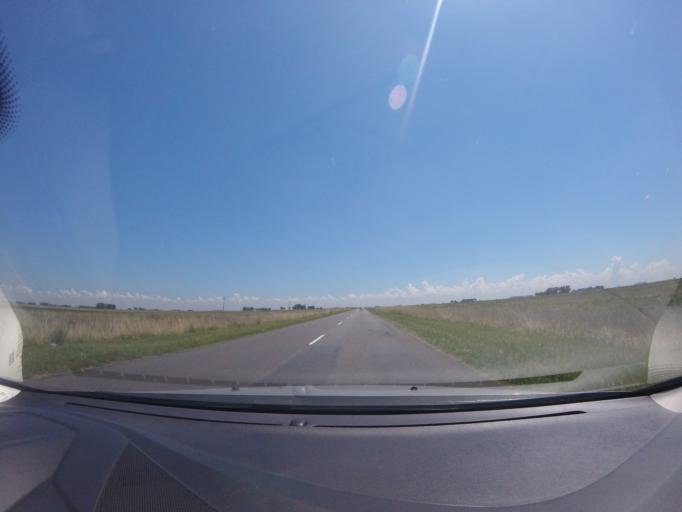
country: AR
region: Buenos Aires
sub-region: Partido de Rauch
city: Rauch
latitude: -36.3971
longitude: -59.0002
